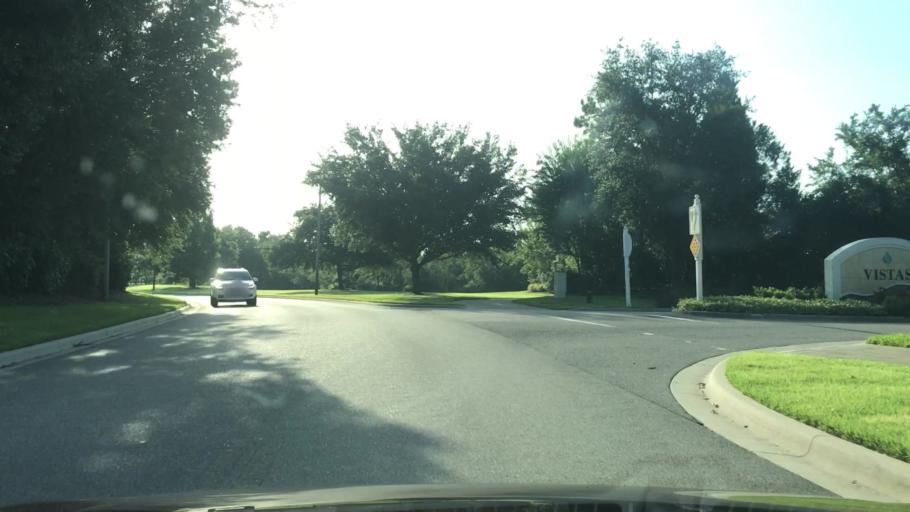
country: US
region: Florida
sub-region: Sarasota County
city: The Meadows
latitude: 27.4379
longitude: -82.4182
